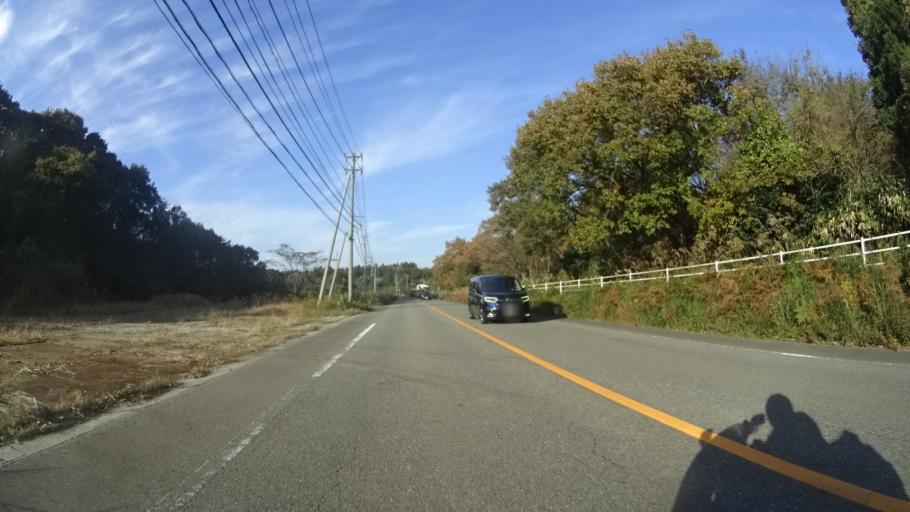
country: JP
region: Ishikawa
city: Hakui
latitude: 37.0537
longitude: 136.7764
